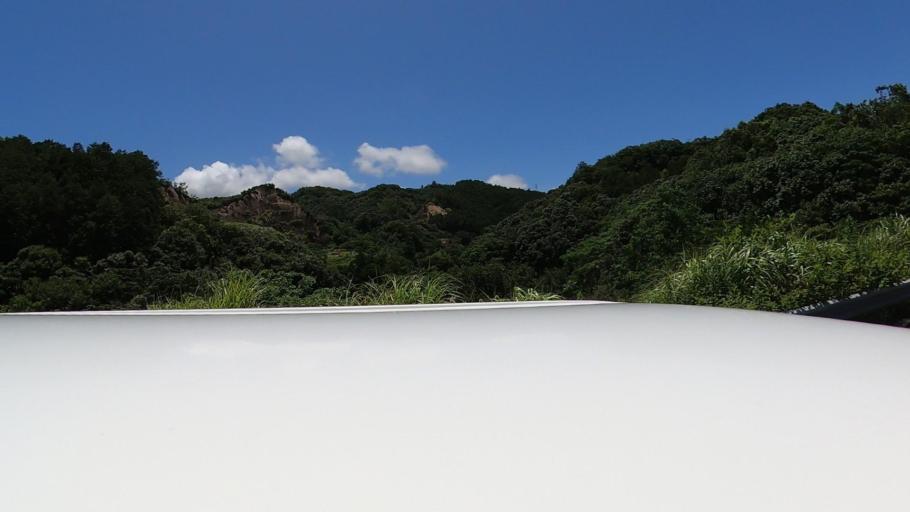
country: JP
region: Miyazaki
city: Nobeoka
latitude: 32.5377
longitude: 131.6598
